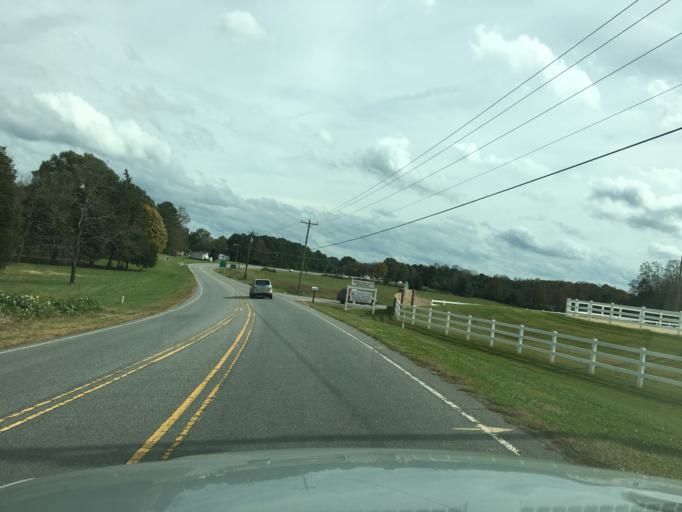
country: US
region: North Carolina
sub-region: Catawba County
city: Newton
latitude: 35.6597
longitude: -81.2708
